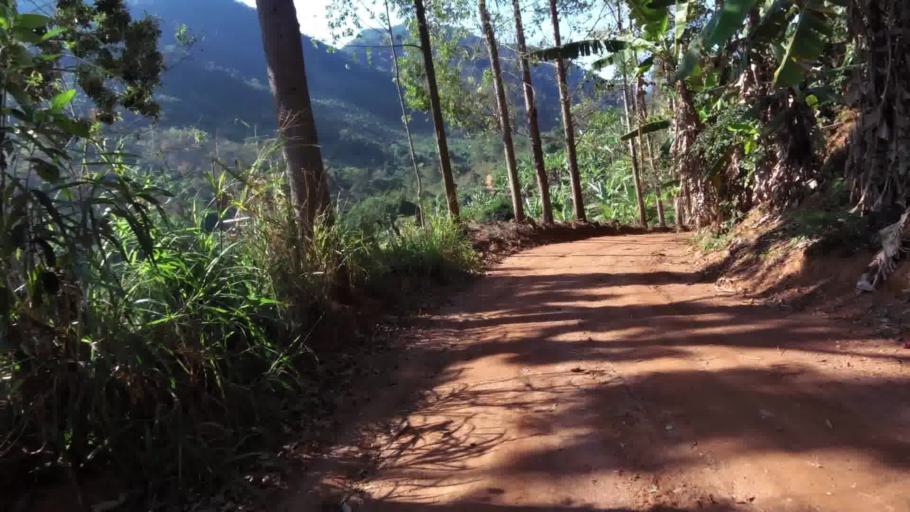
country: BR
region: Espirito Santo
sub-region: Alfredo Chaves
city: Alfredo Chaves
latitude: -20.6036
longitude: -40.7627
